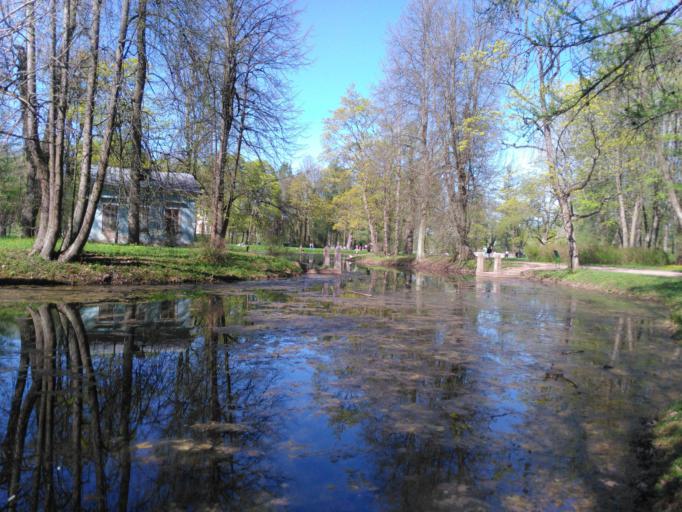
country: RU
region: St.-Petersburg
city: Pushkin
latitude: 59.7210
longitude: 30.3896
